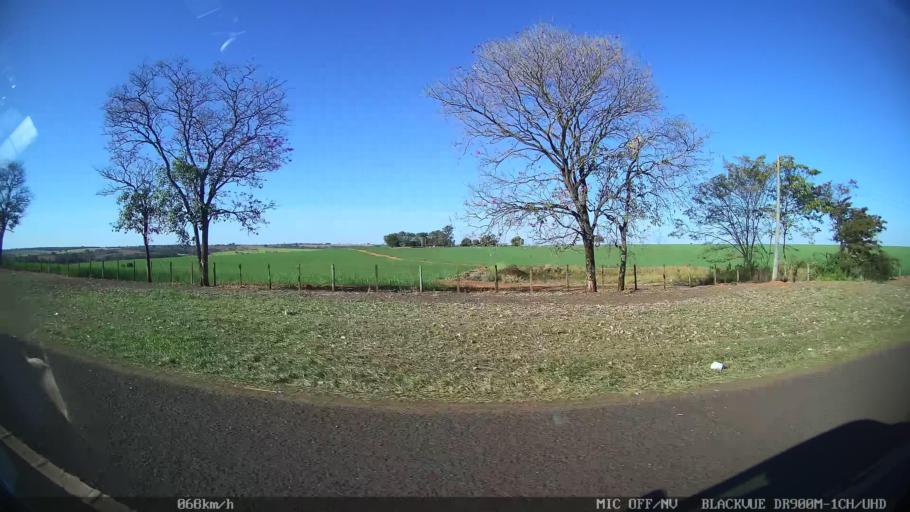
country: BR
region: Sao Paulo
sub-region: Olimpia
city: Olimpia
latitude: -20.7039
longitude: -48.9125
